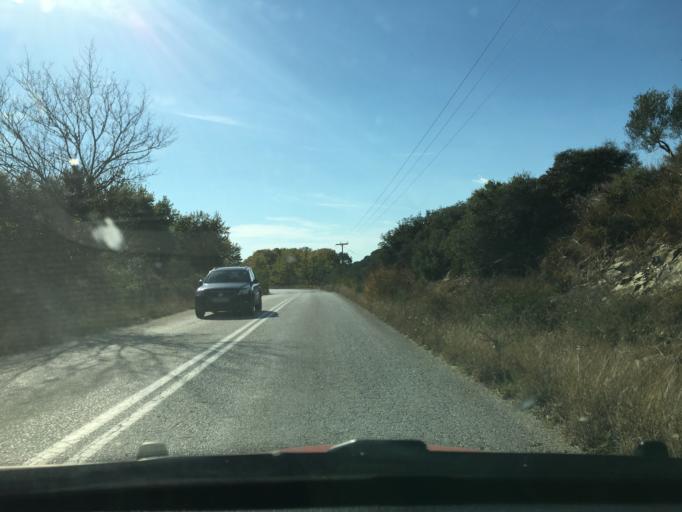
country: GR
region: Central Macedonia
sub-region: Nomos Chalkidikis
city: Megali Panagia
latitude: 40.3833
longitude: 23.7050
